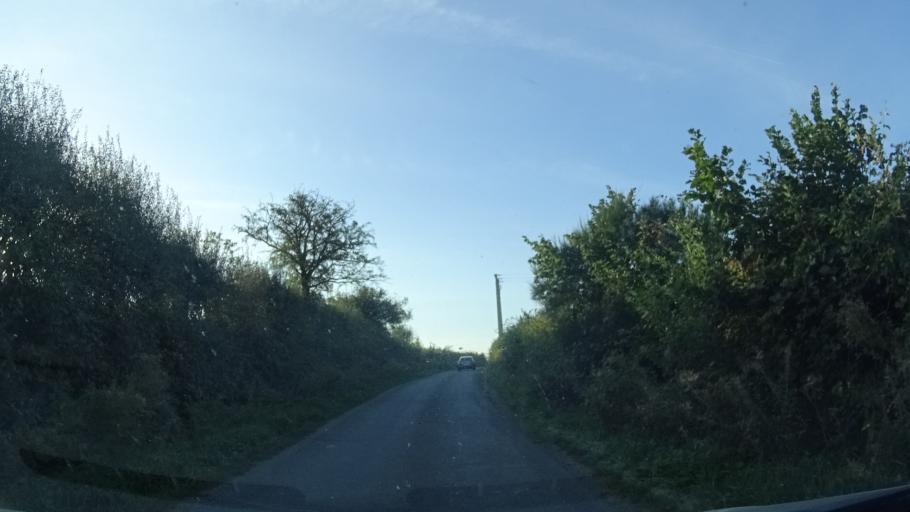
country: BE
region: Wallonia
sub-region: Province du Hainaut
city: Beaumont
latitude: 50.2405
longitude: 4.2689
